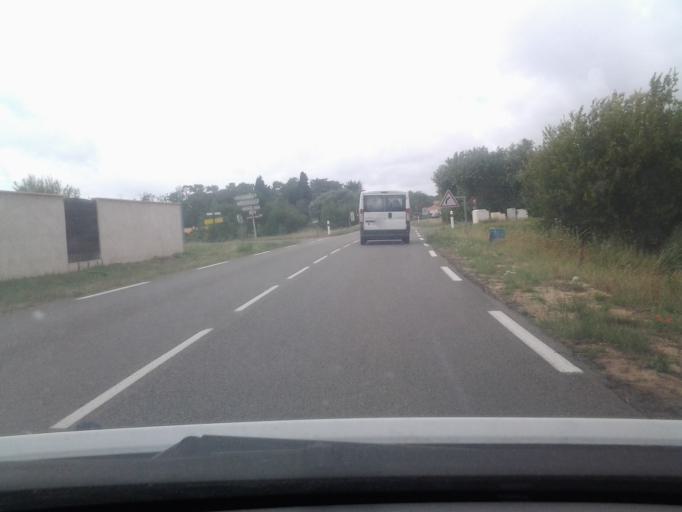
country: FR
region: Pays de la Loire
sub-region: Departement de la Vendee
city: Longeville-sur-Mer
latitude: 46.3931
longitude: -1.4829
